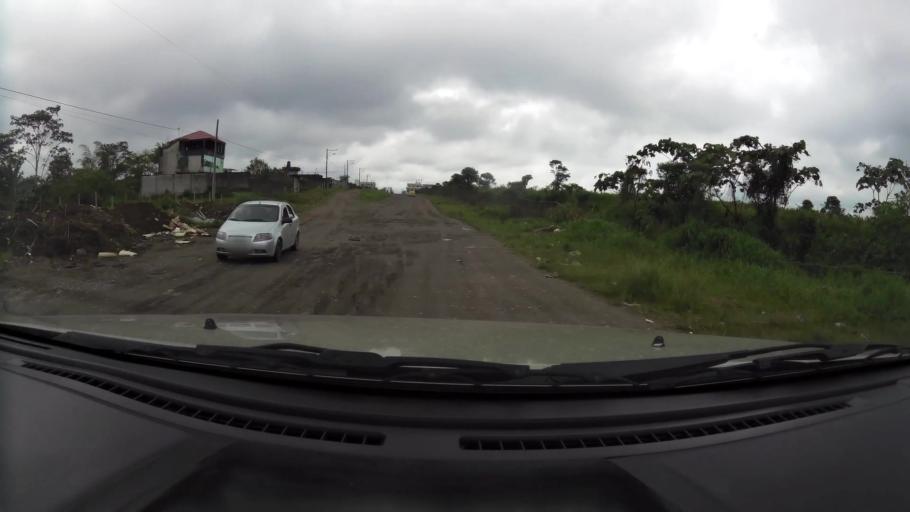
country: EC
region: Santo Domingo de los Tsachilas
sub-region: Canton Santo Domingo de los Colorados
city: Santo Domingo de los Colorados
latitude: -0.2425
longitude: -79.1604
